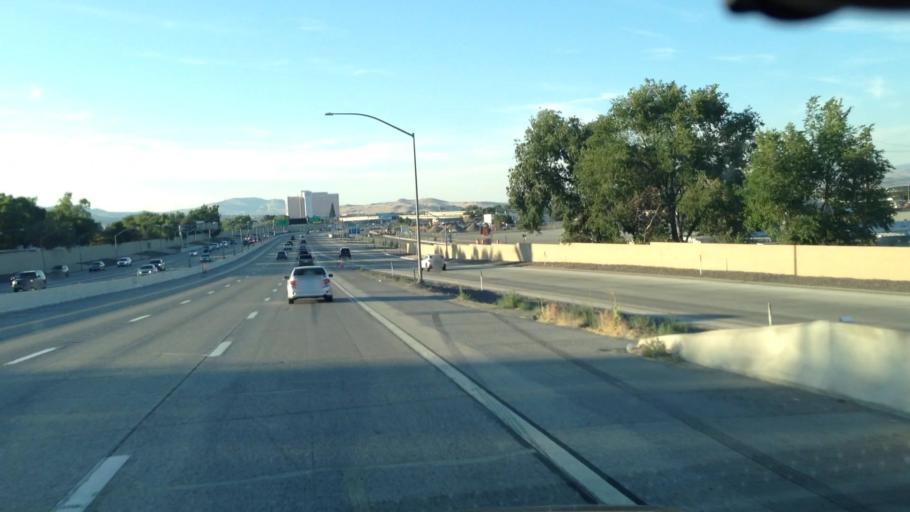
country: US
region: Nevada
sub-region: Washoe County
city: Reno
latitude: 39.4940
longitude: -119.7842
